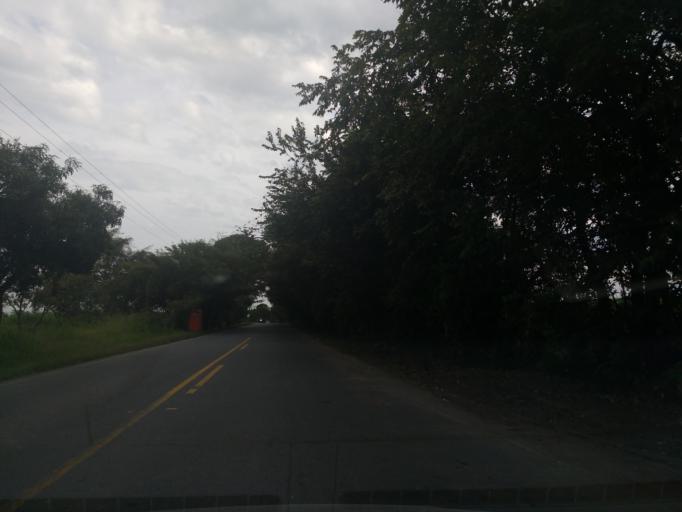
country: CO
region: Valle del Cauca
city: Florida
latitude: 3.2918
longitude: -76.2277
